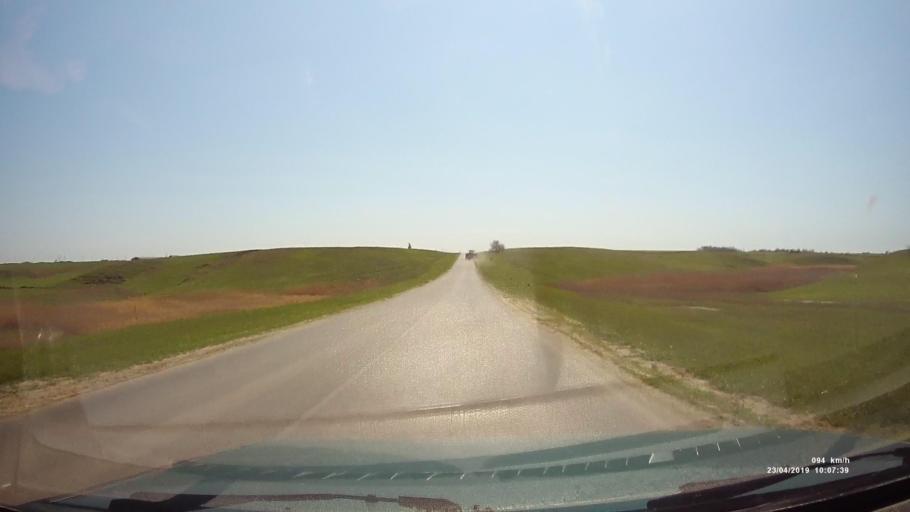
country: RU
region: Rostov
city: Sovetskoye
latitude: 46.7235
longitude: 42.2569
